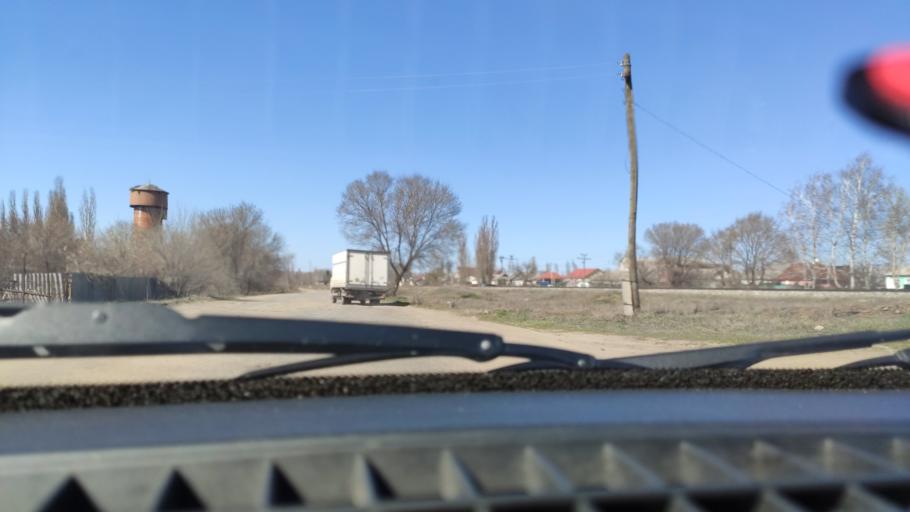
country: RU
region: Voronezj
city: Pridonskoy
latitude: 51.6798
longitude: 39.0732
